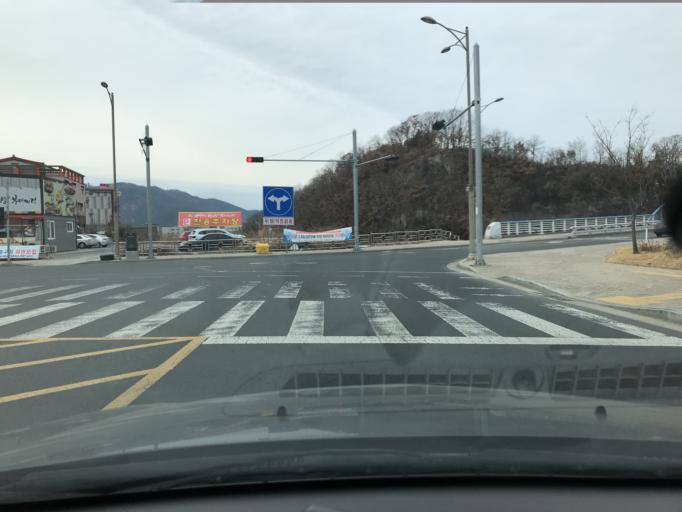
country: KR
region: Daegu
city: Hwawon
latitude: 35.6984
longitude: 128.4546
